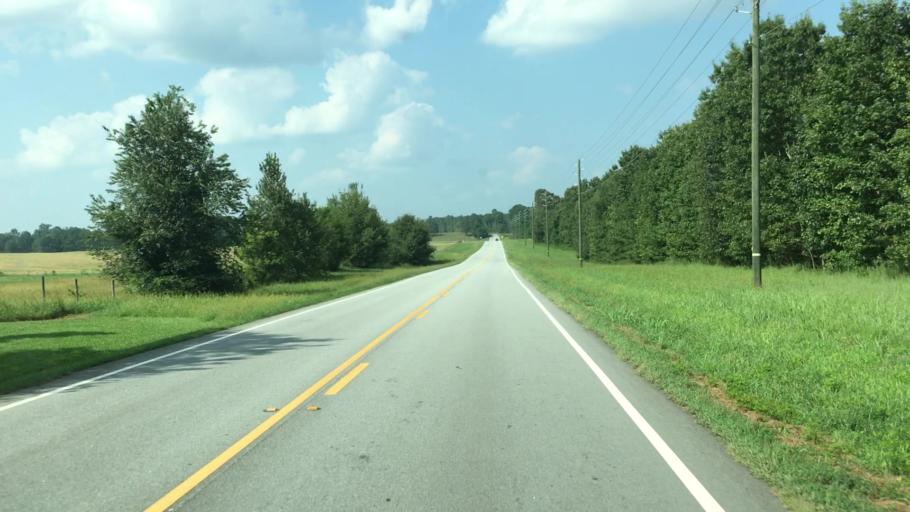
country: US
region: Georgia
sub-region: Jasper County
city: Monticello
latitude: 33.4476
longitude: -83.7557
